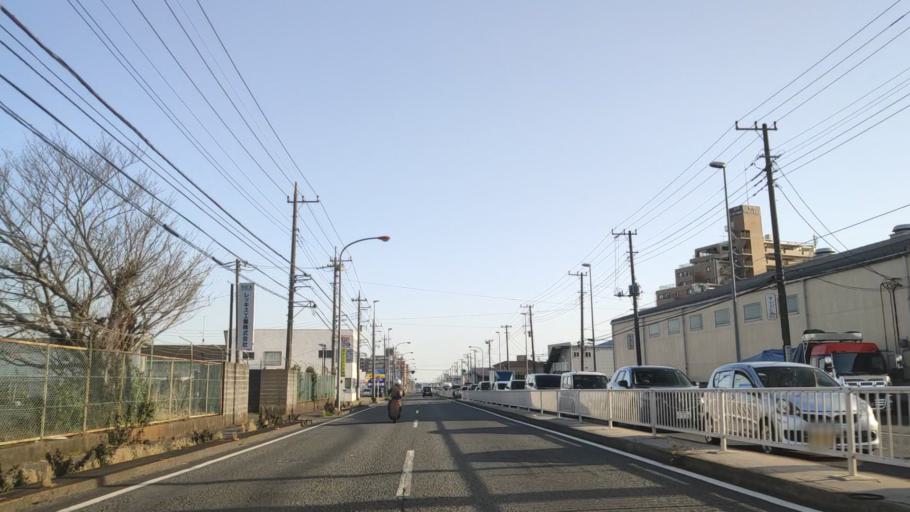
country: JP
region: Kanagawa
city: Zama
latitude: 35.4843
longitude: 139.3654
